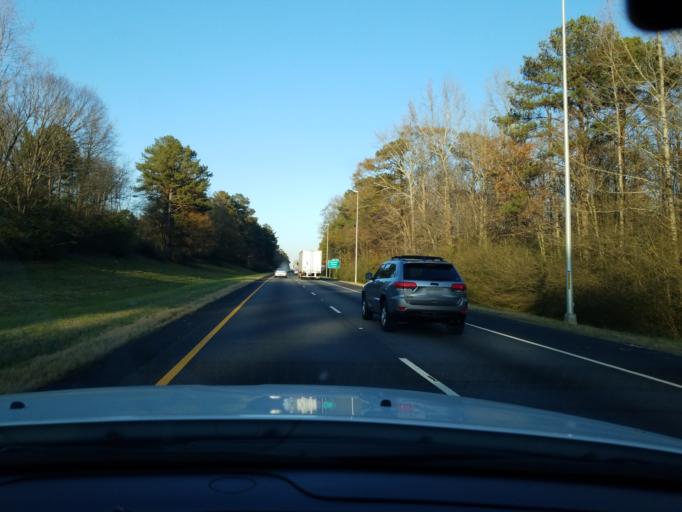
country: US
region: Alabama
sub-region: Jefferson County
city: Trussville
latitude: 33.6259
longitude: -86.6310
